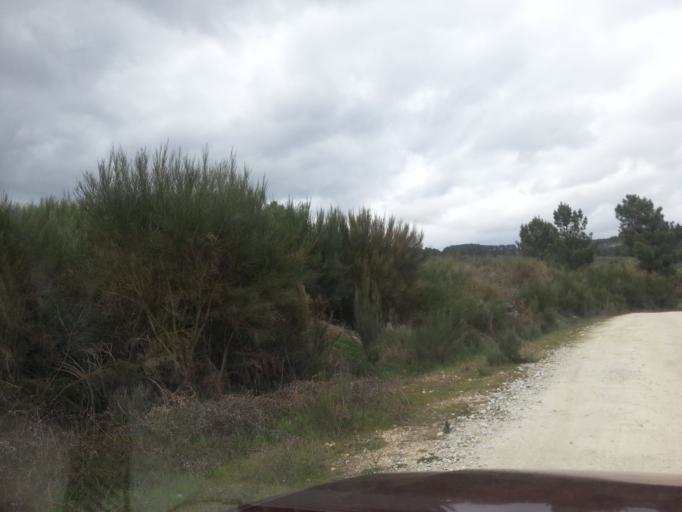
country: PT
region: Guarda
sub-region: Fornos de Algodres
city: Fornos de Algodres
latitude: 40.5977
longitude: -7.5684
